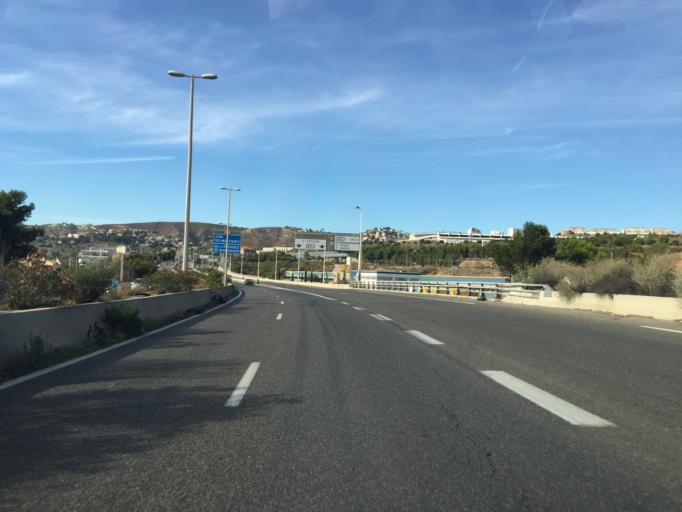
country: FR
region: Provence-Alpes-Cote d'Azur
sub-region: Departement des Bouches-du-Rhone
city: Marseille 16
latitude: 43.3542
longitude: 5.3483
